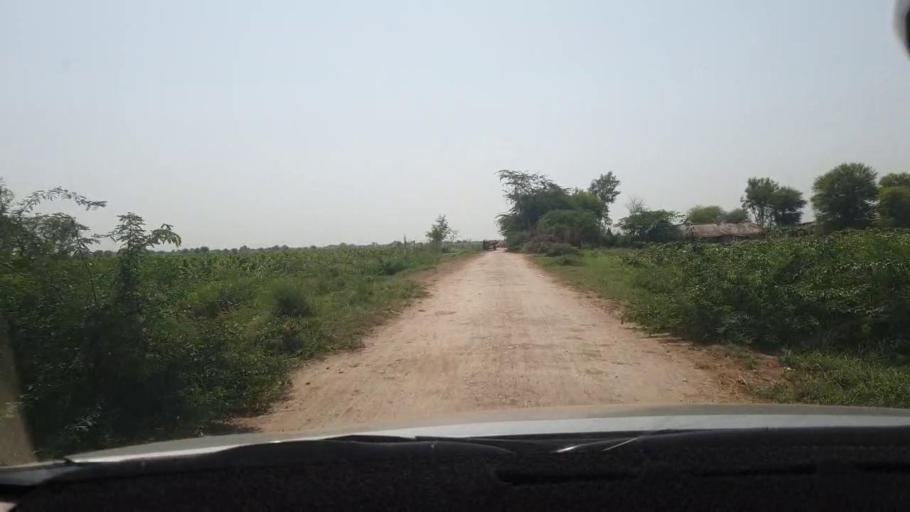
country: PK
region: Sindh
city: Tando Mittha Khan
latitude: 25.8548
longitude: 69.4186
